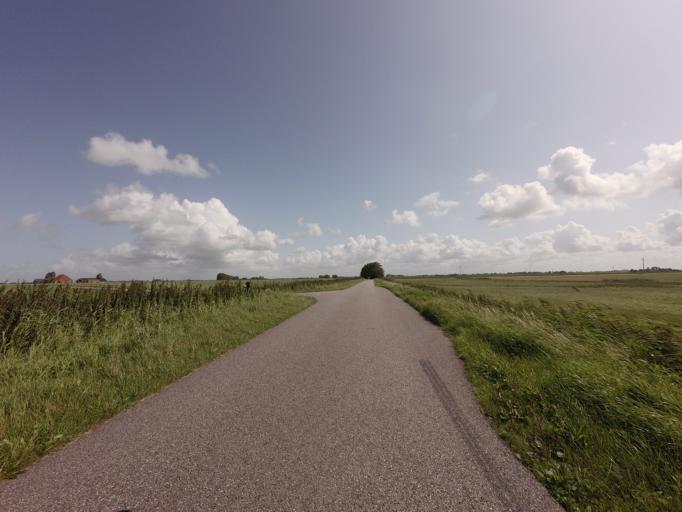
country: NL
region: Friesland
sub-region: Sudwest Fryslan
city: Makkum
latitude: 53.0610
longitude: 5.4305
